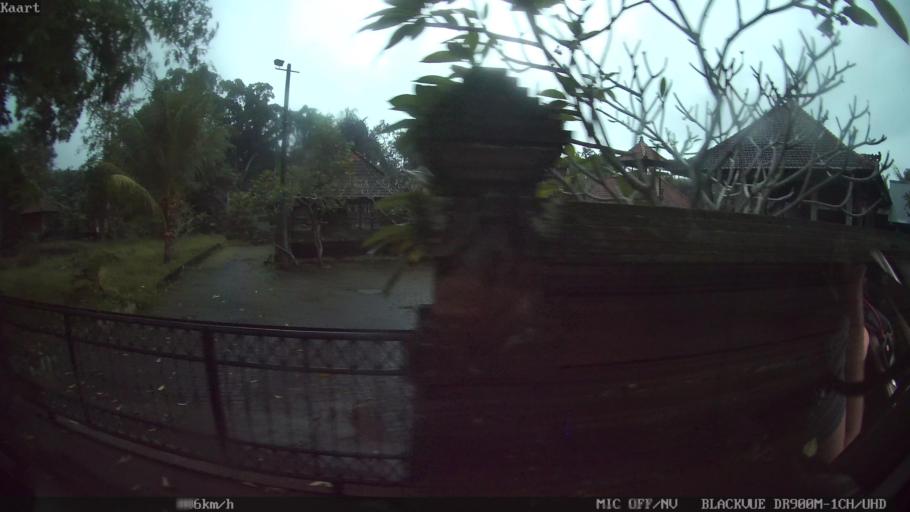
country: ID
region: Bali
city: Banjar Desa
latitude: -8.5747
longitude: 115.2594
